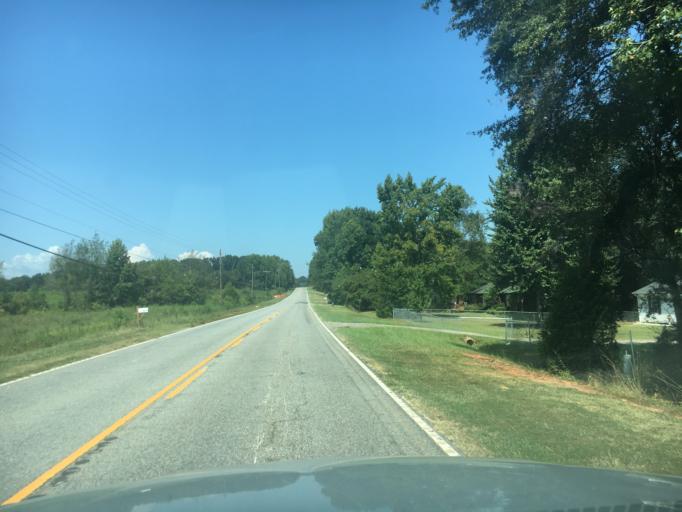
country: US
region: South Carolina
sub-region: Spartanburg County
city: Boiling Springs
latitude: 35.1259
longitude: -82.0322
